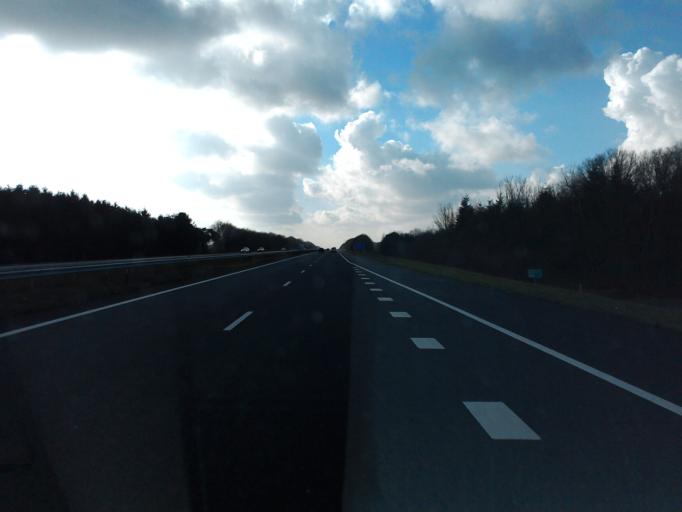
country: NL
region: North Brabant
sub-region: Gemeente Eersel
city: Eersel
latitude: 51.3676
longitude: 5.3118
